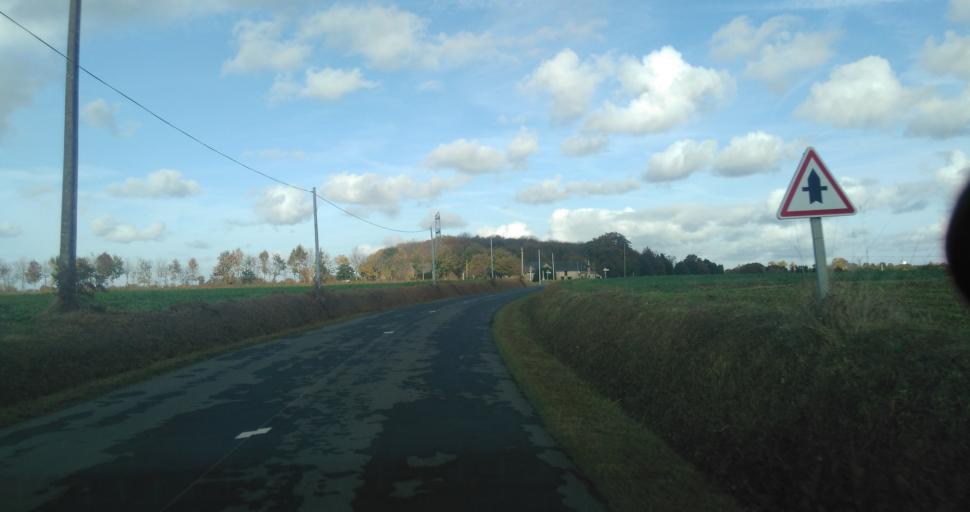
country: FR
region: Brittany
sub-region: Departement d'Ille-et-Vilaine
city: Boisgervilly
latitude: 48.1461
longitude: -2.0797
